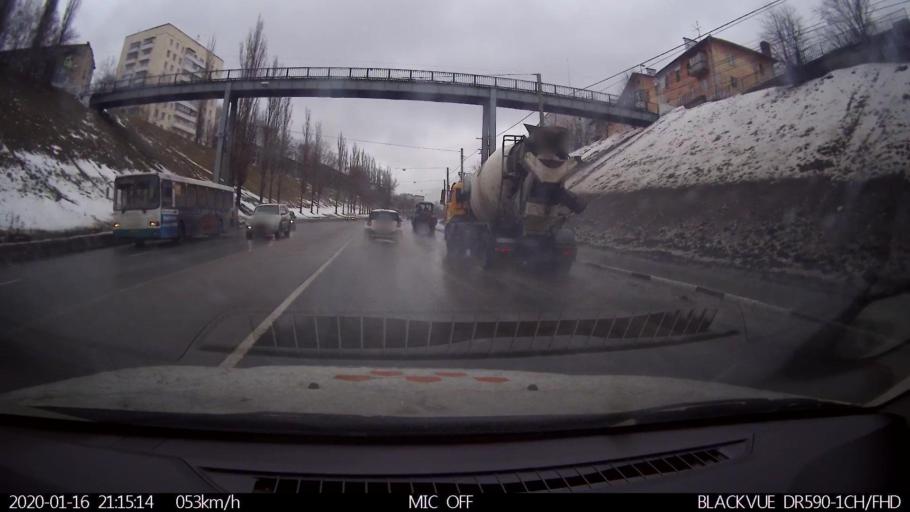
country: RU
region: Nizjnij Novgorod
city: Nizhniy Novgorod
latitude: 56.3202
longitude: 43.9795
